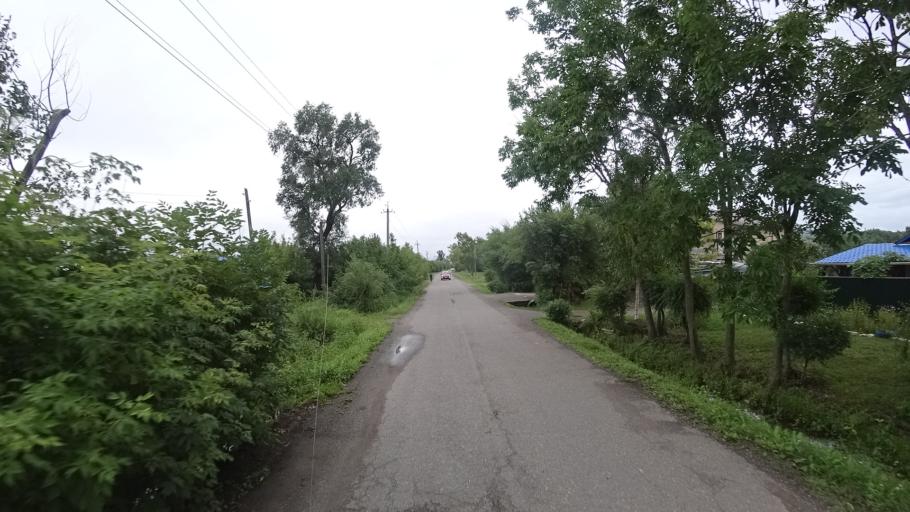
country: RU
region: Primorskiy
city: Chernigovka
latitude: 44.3436
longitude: 132.5840
